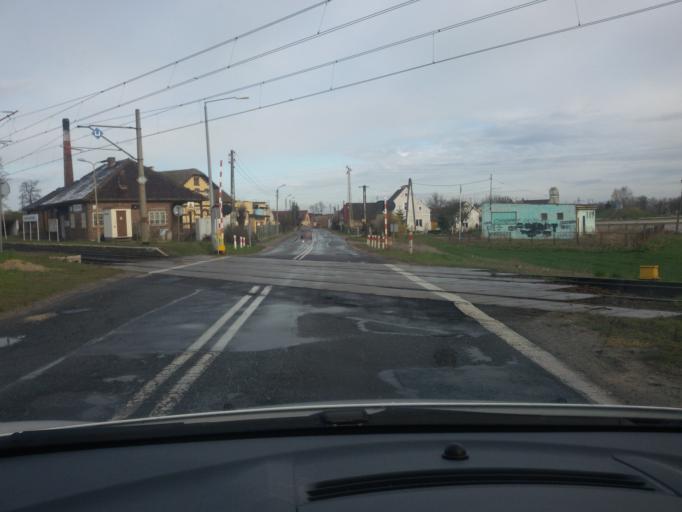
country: PL
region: Lower Silesian Voivodeship
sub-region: Powiat polkowicki
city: Gaworzyce
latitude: 51.6906
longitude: 15.9200
